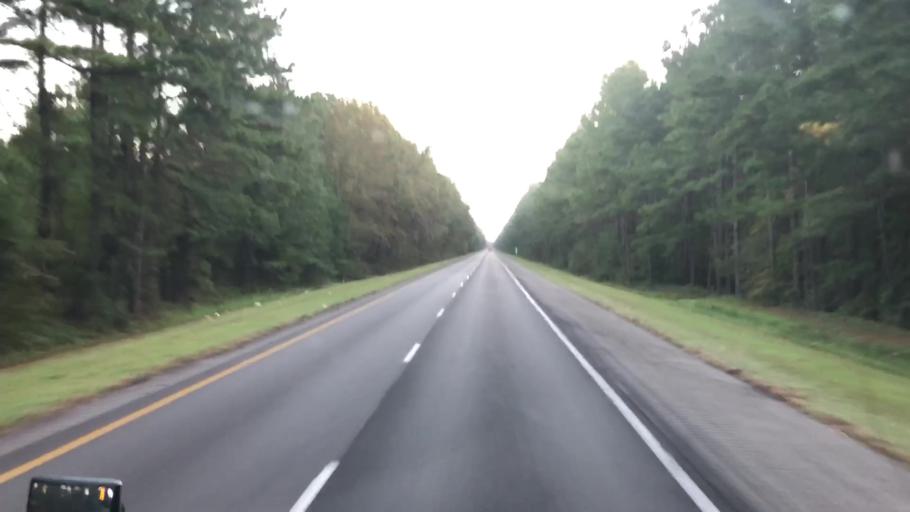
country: US
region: South Carolina
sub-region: Orangeburg County
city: Holly Hill
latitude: 33.5363
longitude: -80.4185
